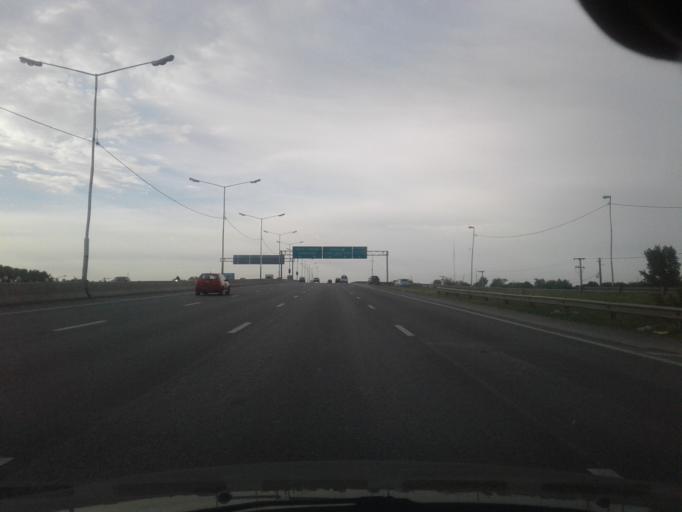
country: AR
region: Santa Fe
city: Perez
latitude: -32.9502
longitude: -60.7220
